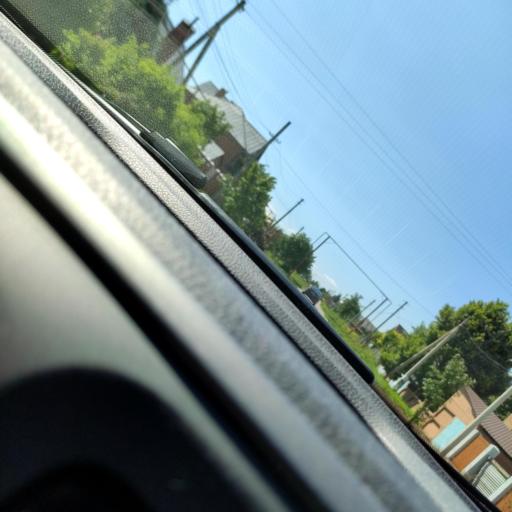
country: RU
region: Samara
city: Podstepki
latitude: 53.5219
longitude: 49.1507
